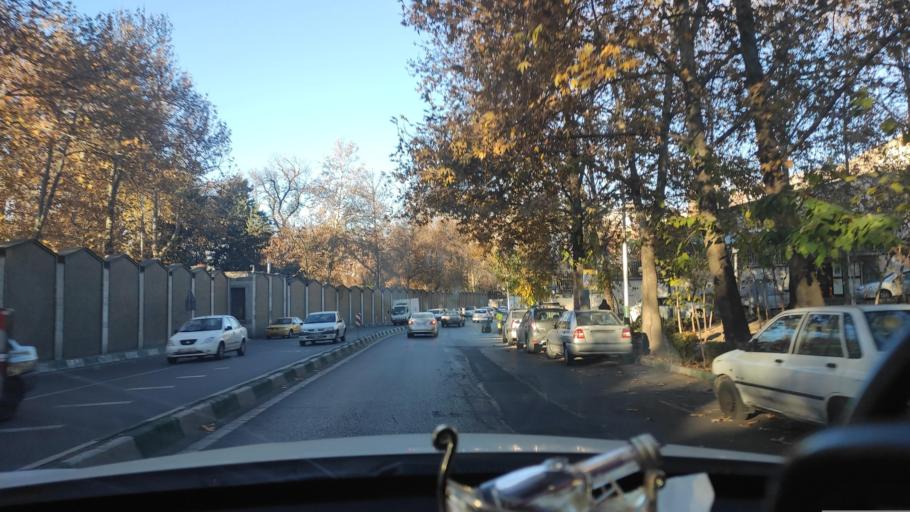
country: IR
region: Tehran
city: Tajrish
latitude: 35.8130
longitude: 51.4731
